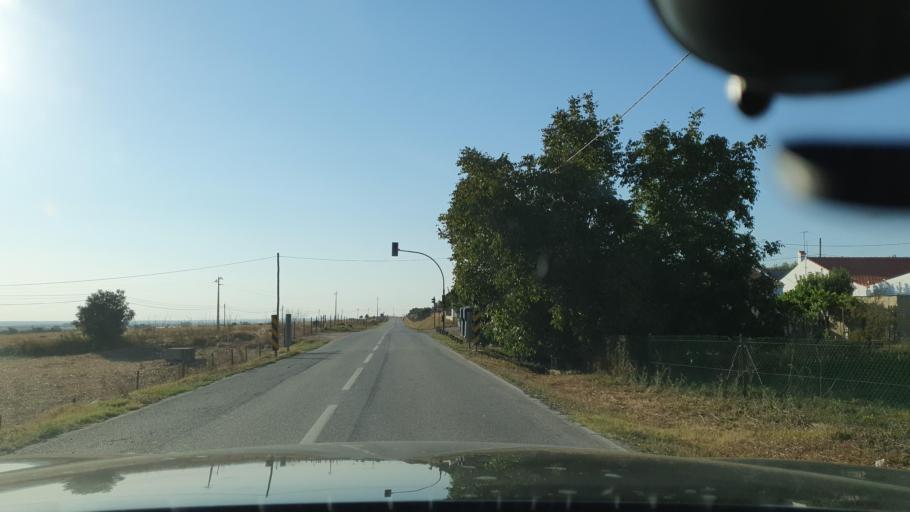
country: PT
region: Evora
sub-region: Estremoz
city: Estremoz
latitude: 38.8784
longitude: -7.6389
